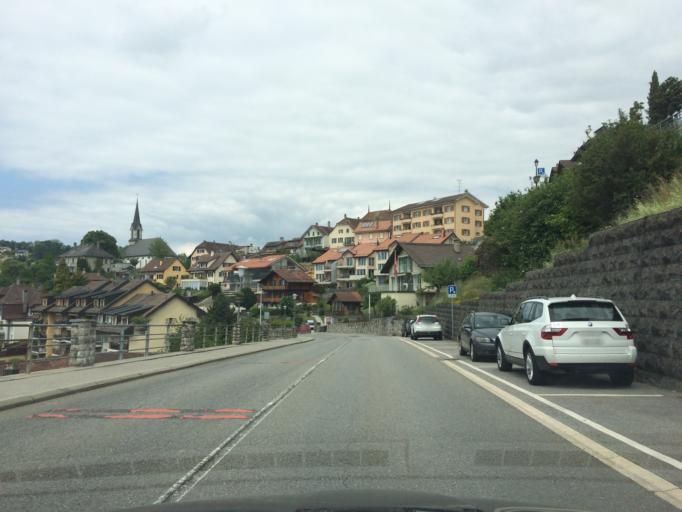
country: CH
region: Vaud
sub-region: Lavaux-Oron District
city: Chexbres
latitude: 46.4817
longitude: 6.7809
